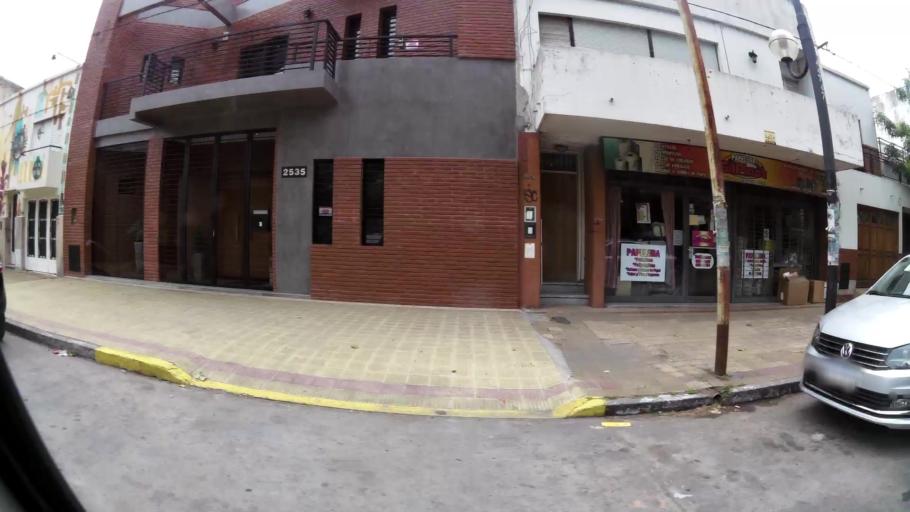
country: AR
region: Buenos Aires
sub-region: Partido de La Plata
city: La Plata
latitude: -34.9346
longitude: -57.9539
